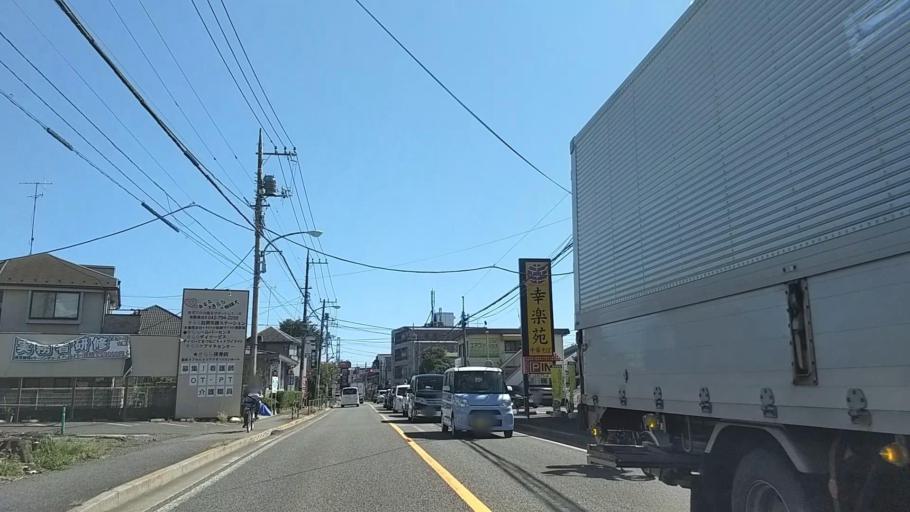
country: JP
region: Tokyo
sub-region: Machida-shi
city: Machida
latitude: 35.5688
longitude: 139.4225
